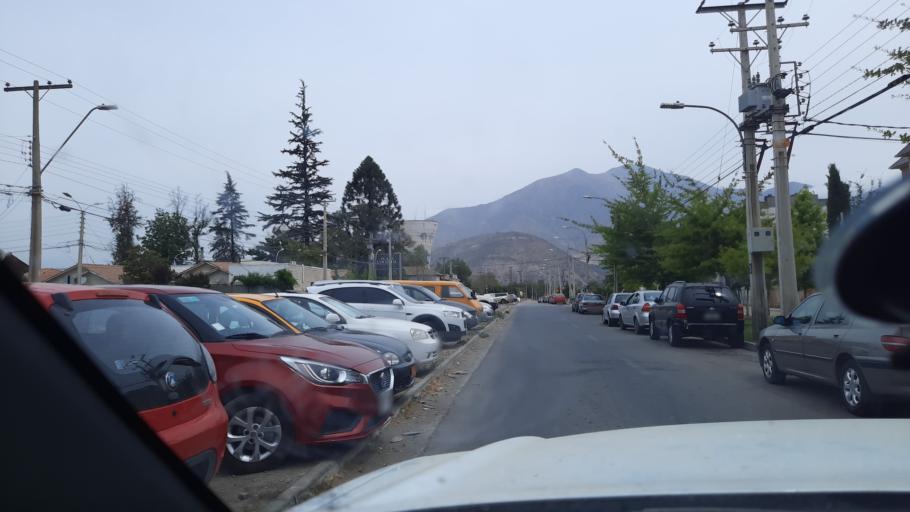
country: CL
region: Valparaiso
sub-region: Provincia de San Felipe
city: San Felipe
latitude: -32.7586
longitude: -70.7226
